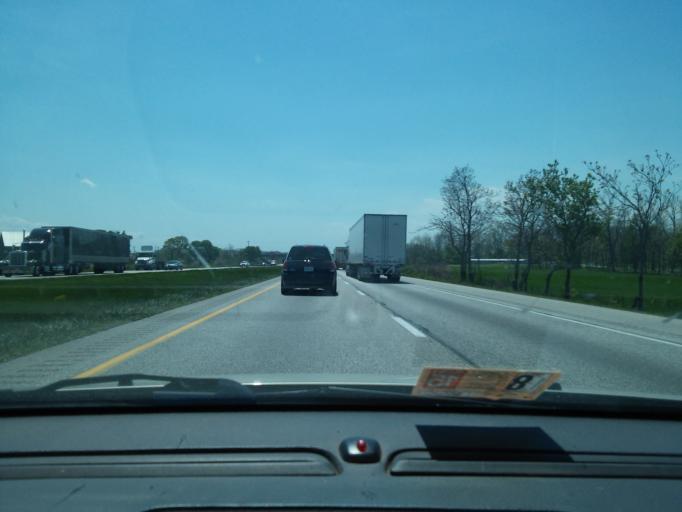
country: US
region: Pennsylvania
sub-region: Franklin County
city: Chambersburg
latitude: 39.8801
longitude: -77.6759
